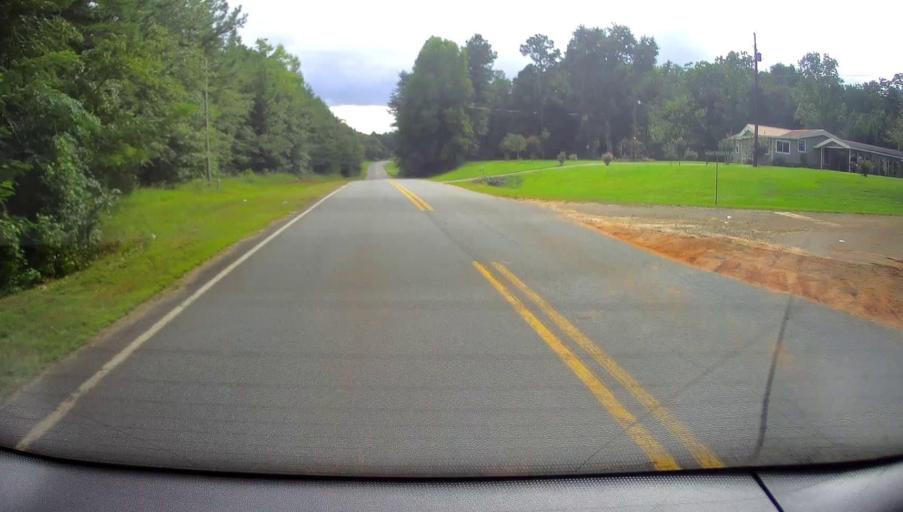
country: US
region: Georgia
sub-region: Meriwether County
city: Manchester
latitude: 32.9674
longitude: -84.5965
